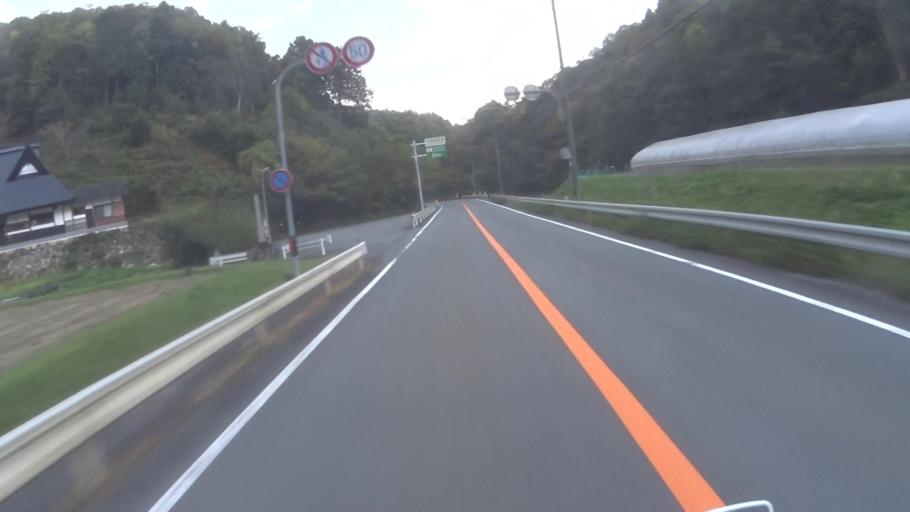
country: JP
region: Kyoto
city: Ayabe
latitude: 35.2301
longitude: 135.3345
